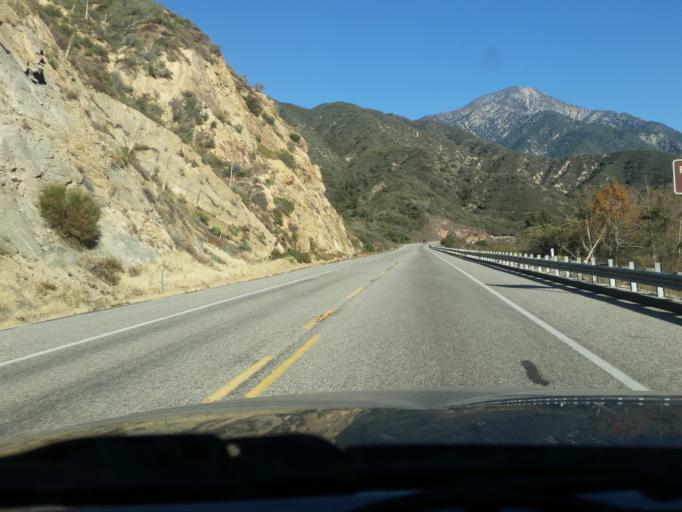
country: US
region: California
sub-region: San Bernardino County
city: Yucaipa
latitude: 34.1030
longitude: -117.0186
